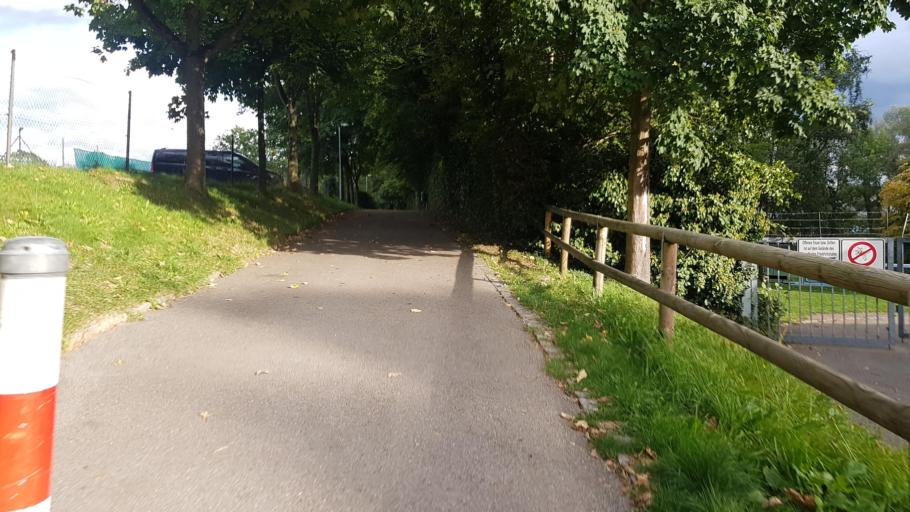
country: DE
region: Baden-Wuerttemberg
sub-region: Tuebingen Region
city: Friedrichshafen
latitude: 47.6529
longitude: 9.4579
